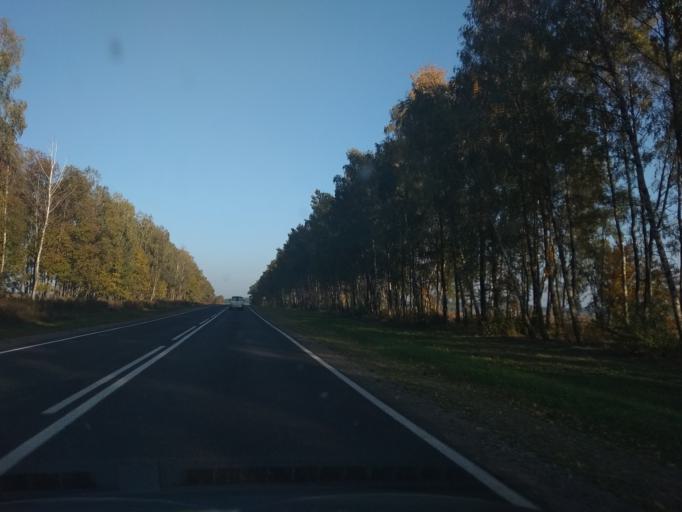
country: BY
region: Grodnenskaya
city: Vawkavysk
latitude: 53.1401
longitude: 24.3314
